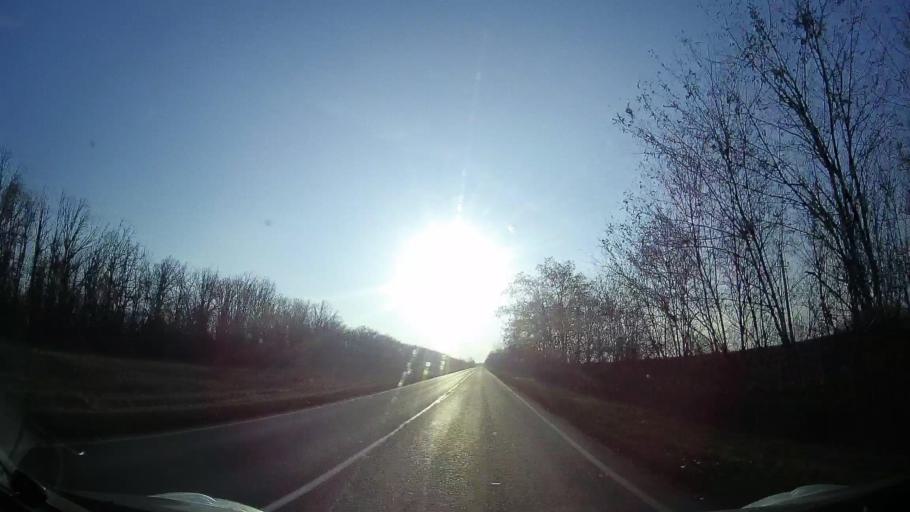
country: RU
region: Rostov
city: Ol'ginskaya
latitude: 47.1586
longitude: 39.9262
